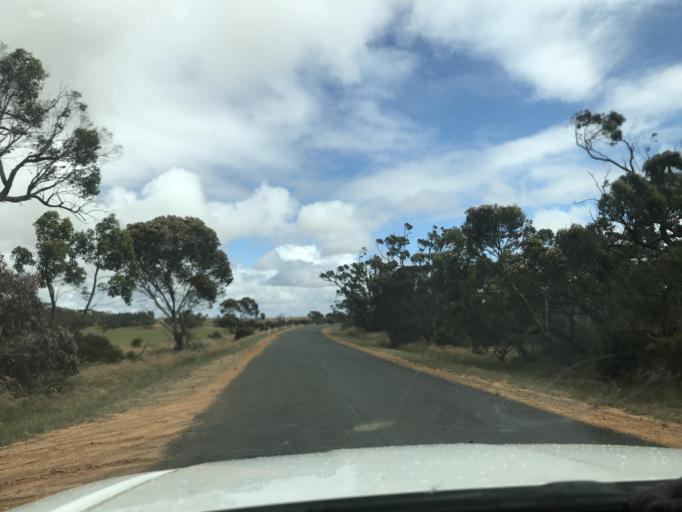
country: AU
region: South Australia
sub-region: Tatiara
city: Bordertown
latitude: -36.1975
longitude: 141.1596
